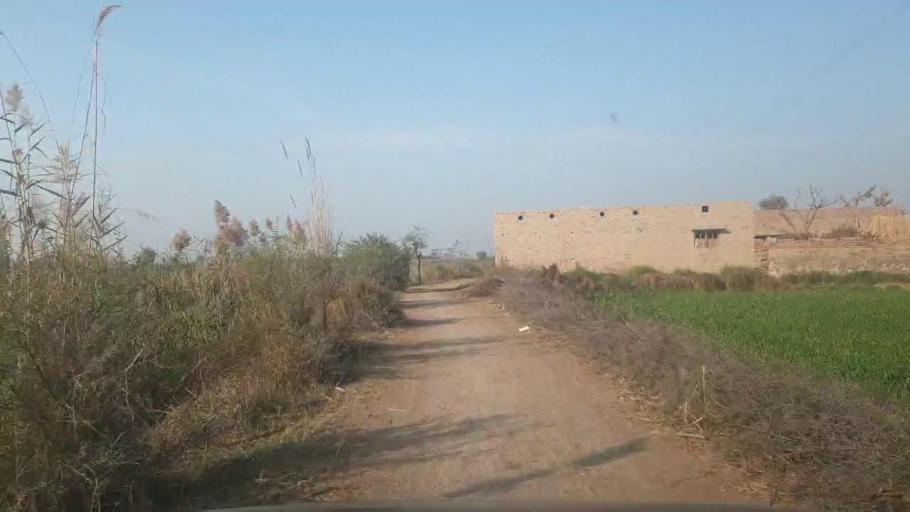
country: PK
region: Sindh
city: Sakrand
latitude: 26.0697
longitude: 68.3453
